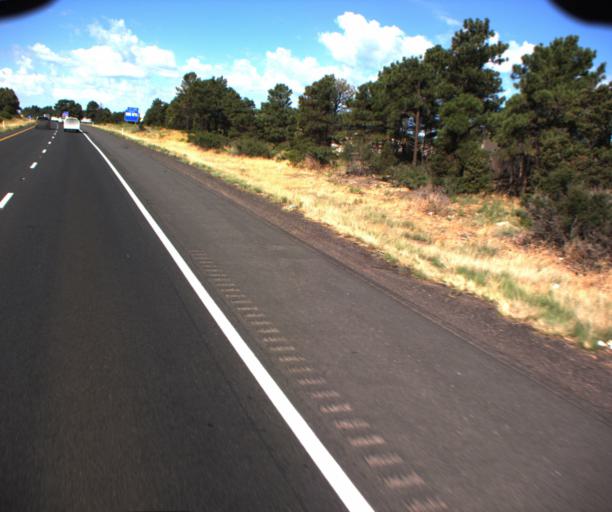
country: US
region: Arizona
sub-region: Coconino County
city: Flagstaff
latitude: 35.2111
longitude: -111.5962
